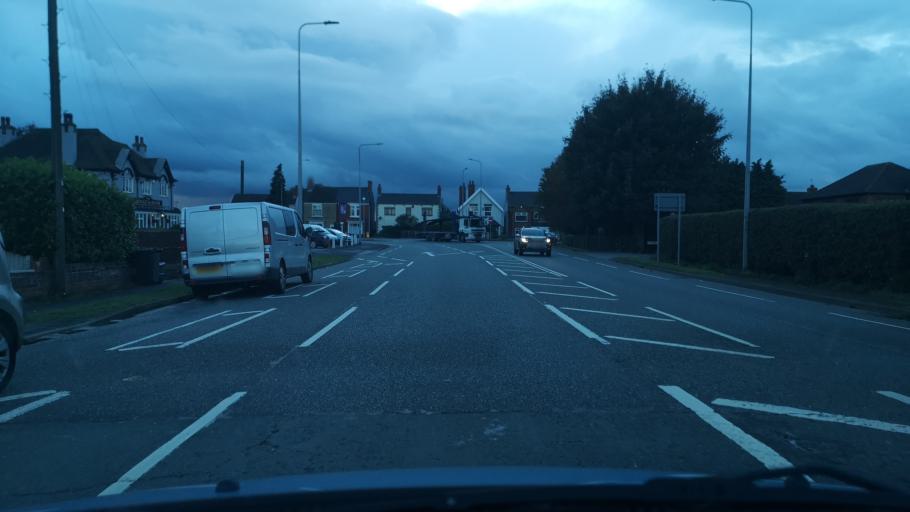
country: GB
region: England
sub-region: North Lincolnshire
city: Gunness
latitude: 53.5905
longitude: -0.7267
